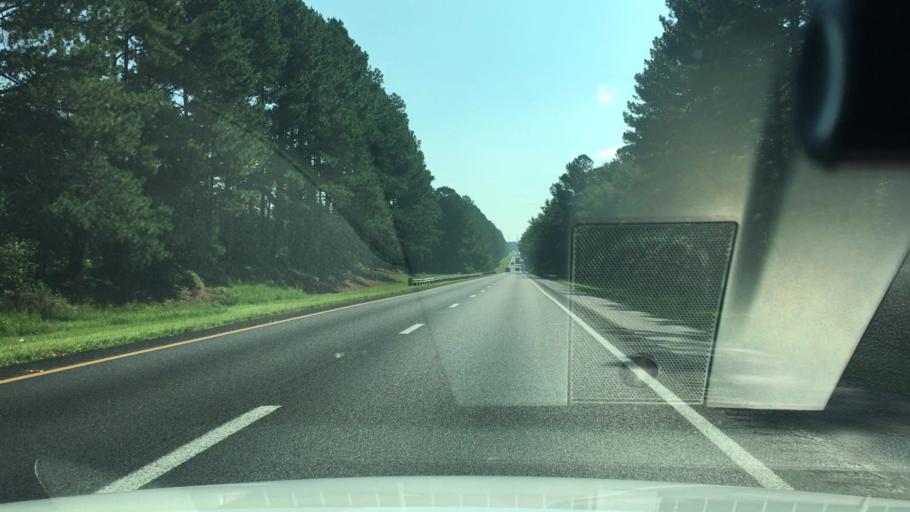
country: US
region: South Carolina
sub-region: Aiken County
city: Graniteville
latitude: 33.6273
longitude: -81.8095
